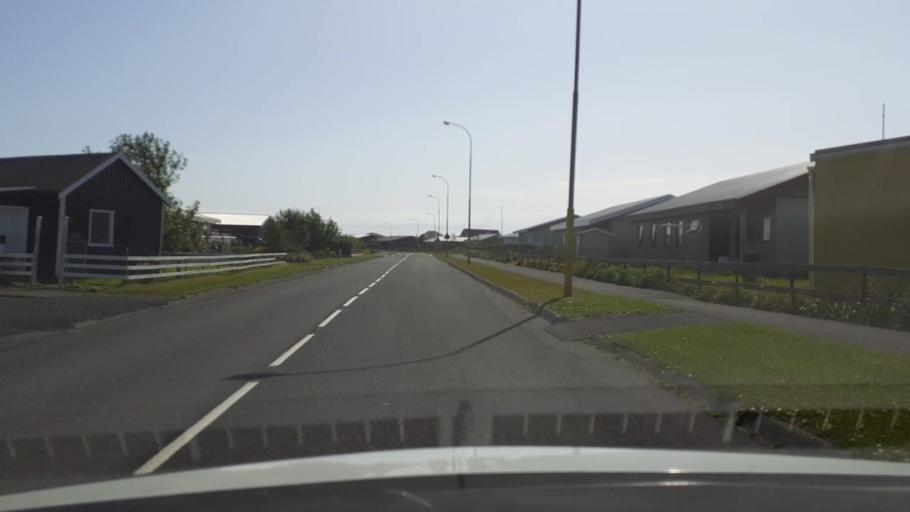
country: IS
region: South
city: Selfoss
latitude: 63.8354
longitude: -21.0603
